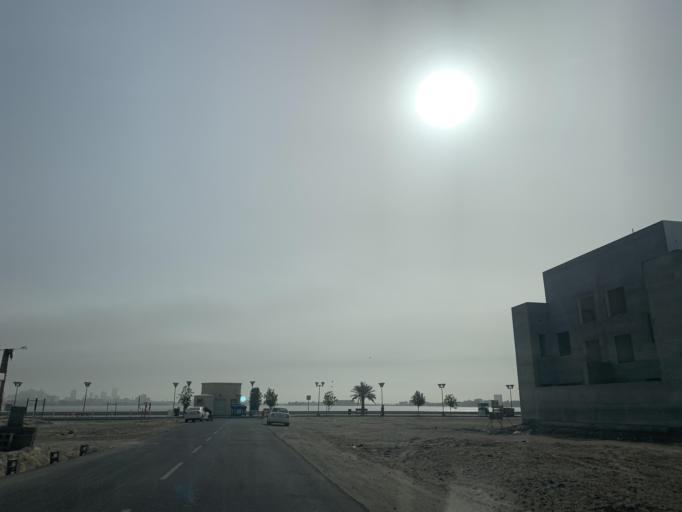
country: BH
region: Northern
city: Madinat `Isa
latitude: 26.1883
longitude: 50.5662
